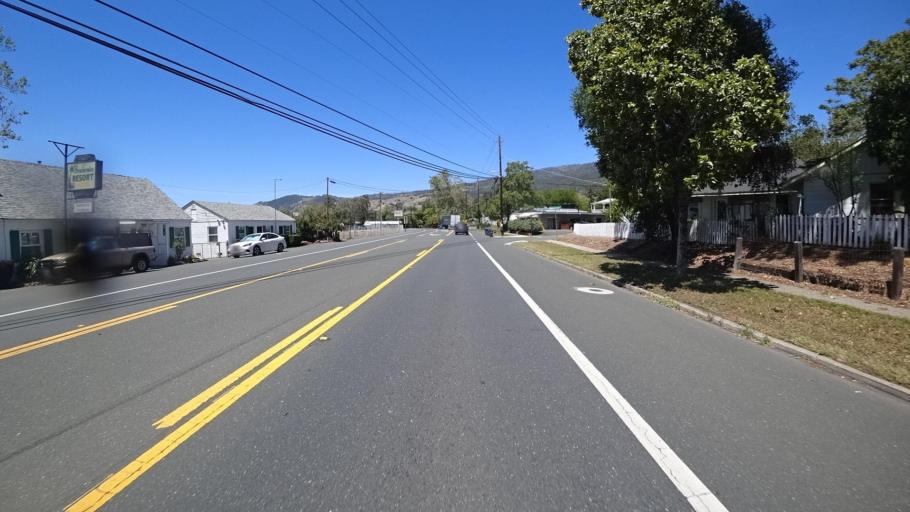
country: US
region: California
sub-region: Lake County
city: Lucerne
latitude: 39.0841
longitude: -122.7912
